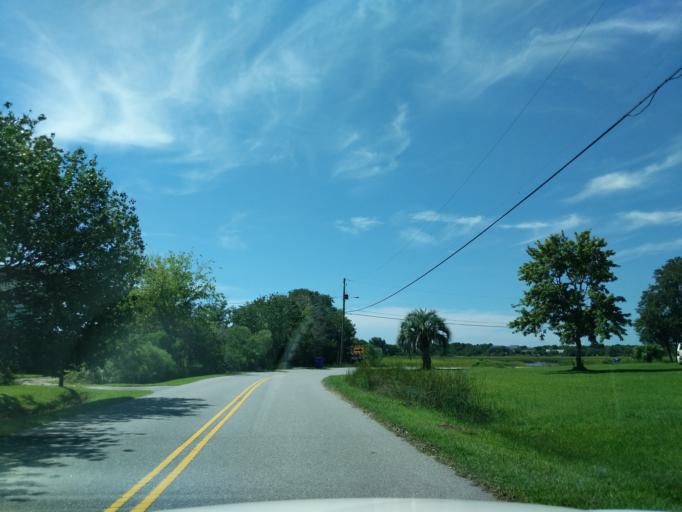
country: US
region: South Carolina
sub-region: Charleston County
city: Folly Beach
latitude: 32.6950
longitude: -79.9579
